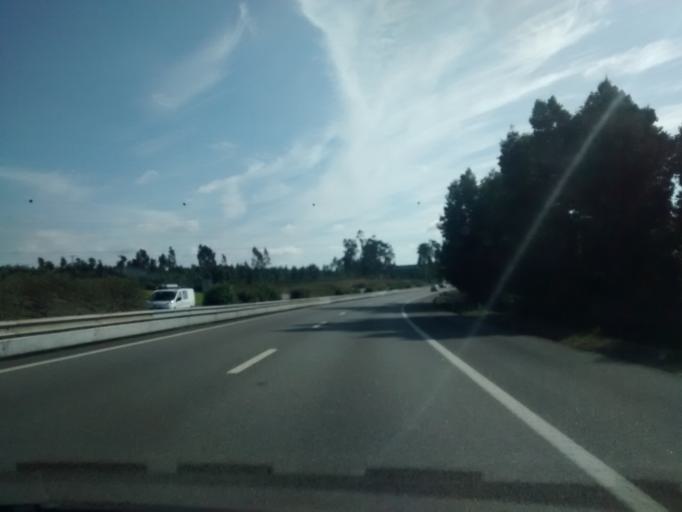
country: PT
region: Porto
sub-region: Santo Tirso
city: Santo Tirso
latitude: 41.3591
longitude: -8.5013
